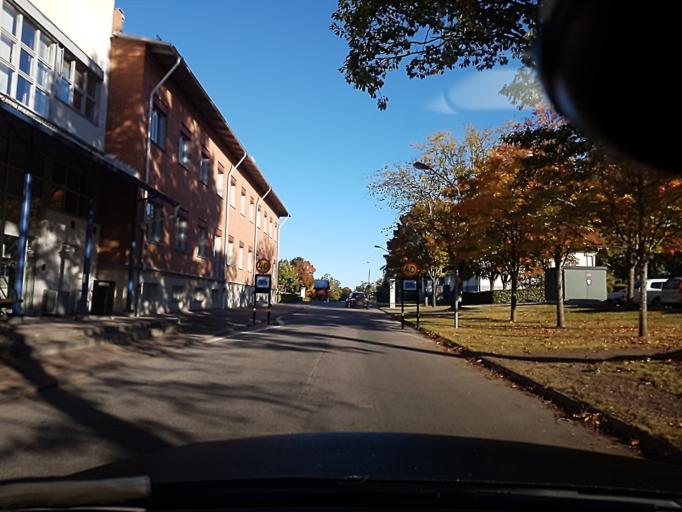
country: SE
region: Kronoberg
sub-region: Vaxjo Kommun
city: Vaexjoe
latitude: 56.8554
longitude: 14.8311
